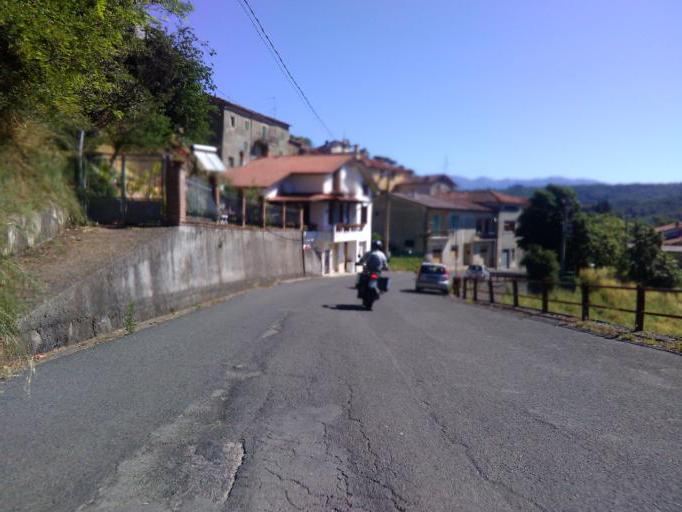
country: IT
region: Tuscany
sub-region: Provincia di Massa-Carrara
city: Fosdinovo
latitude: 44.1726
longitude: 10.0491
